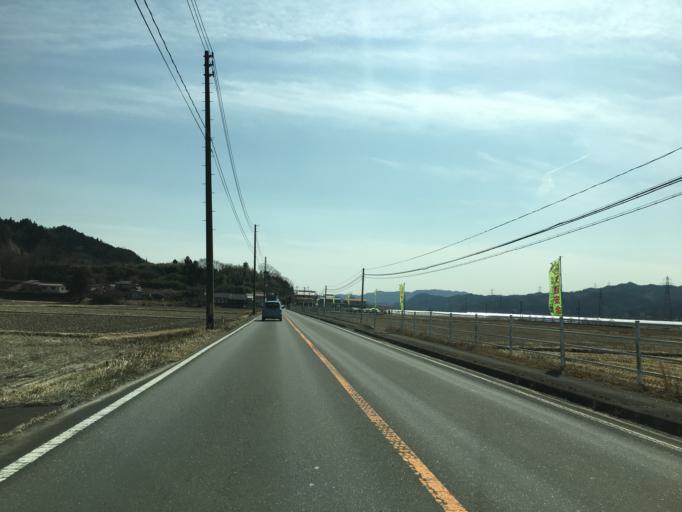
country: JP
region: Ibaraki
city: Daigo
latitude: 36.9195
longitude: 140.4162
